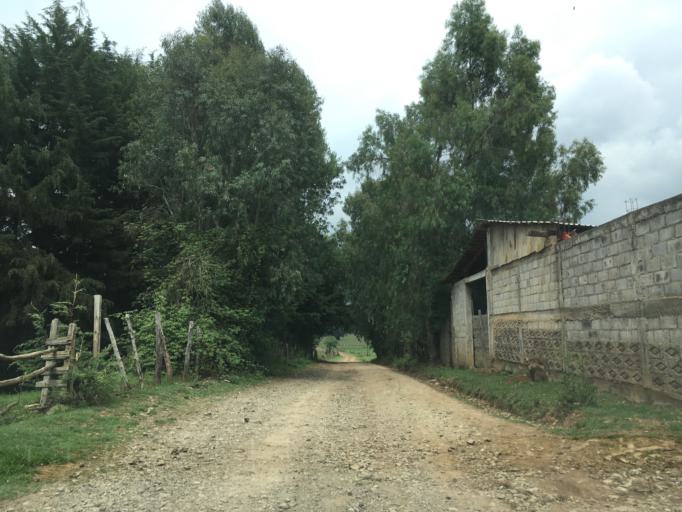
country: MX
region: Michoacan
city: Acuitzio del Canje
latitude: 19.4999
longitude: -101.2263
